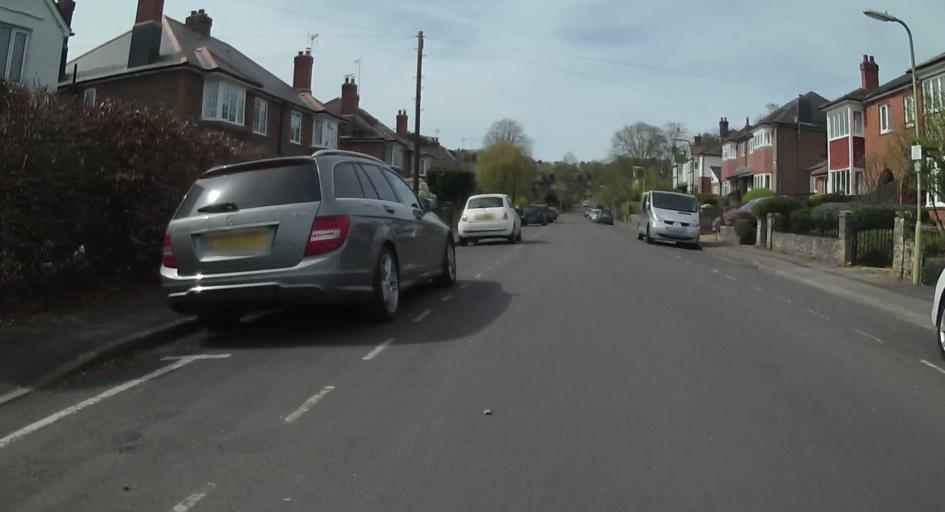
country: GB
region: England
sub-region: Hampshire
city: Winchester
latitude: 51.0678
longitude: -1.3266
